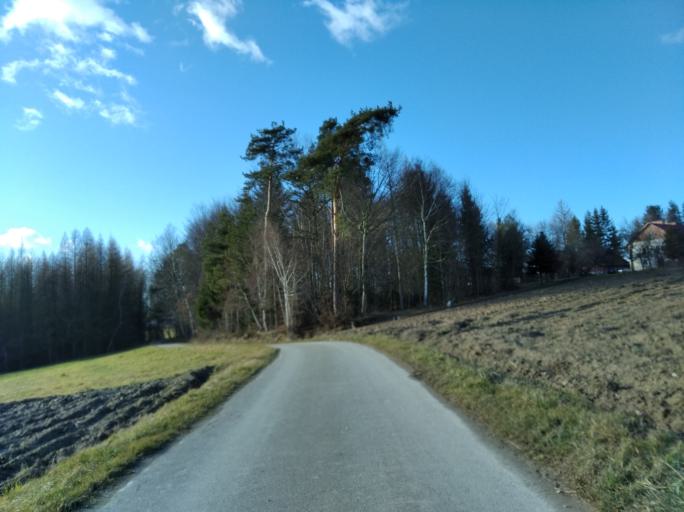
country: PL
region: Subcarpathian Voivodeship
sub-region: Powiat strzyzowski
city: Wisniowa
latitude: 49.9012
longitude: 21.7108
